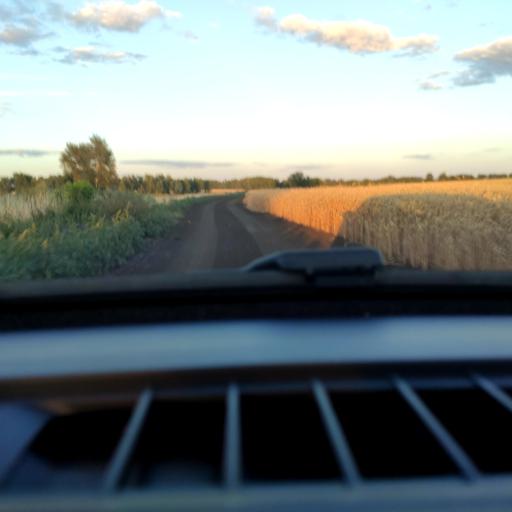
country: RU
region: Voronezj
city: Verkhnyaya Khava
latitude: 51.5898
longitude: 39.8671
